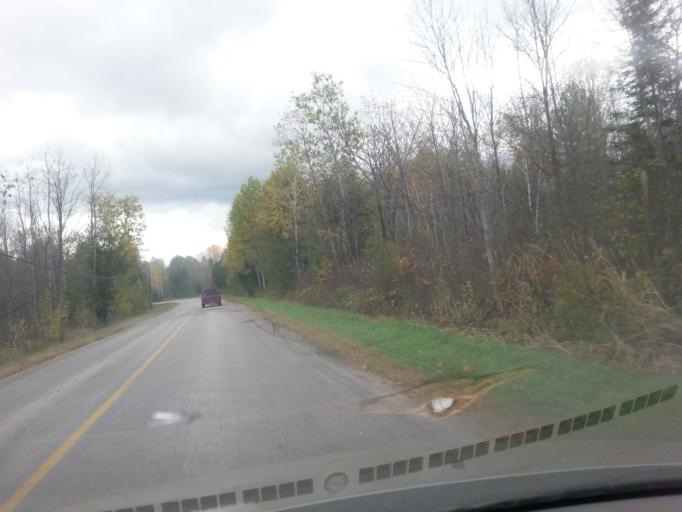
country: CA
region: Ontario
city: Pembroke
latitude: 45.5213
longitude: -77.0708
